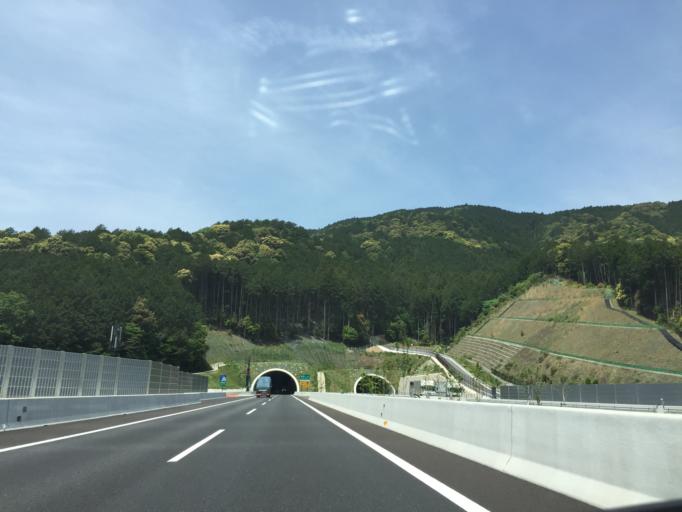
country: JP
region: Aichi
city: Kozakai-cho
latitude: 34.8960
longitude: 137.3314
